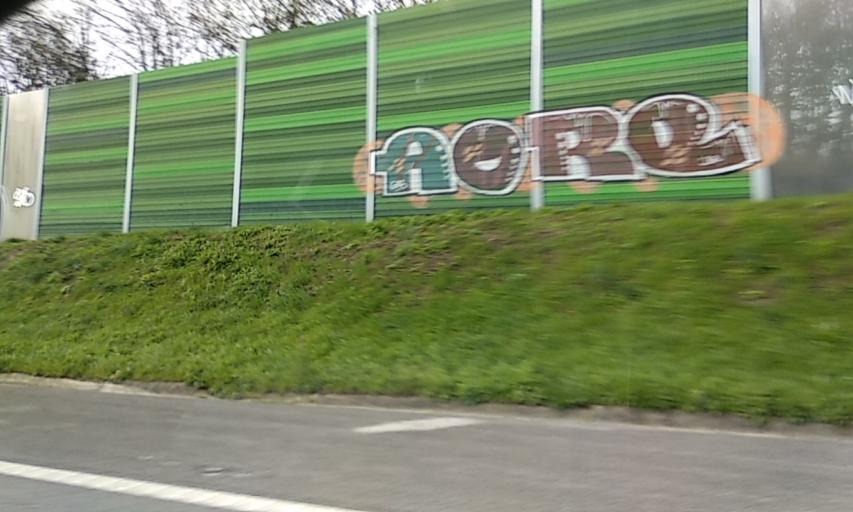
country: PT
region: Porto
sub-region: Santo Tirso
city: Santo Tirso
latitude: 41.3710
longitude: -8.5036
